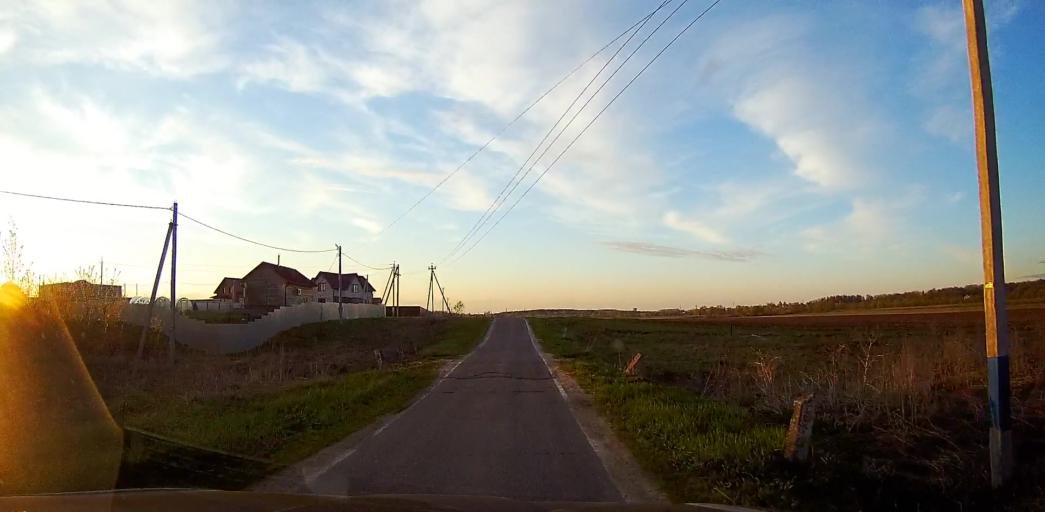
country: RU
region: Moskovskaya
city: Peski
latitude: 55.2134
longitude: 38.7392
